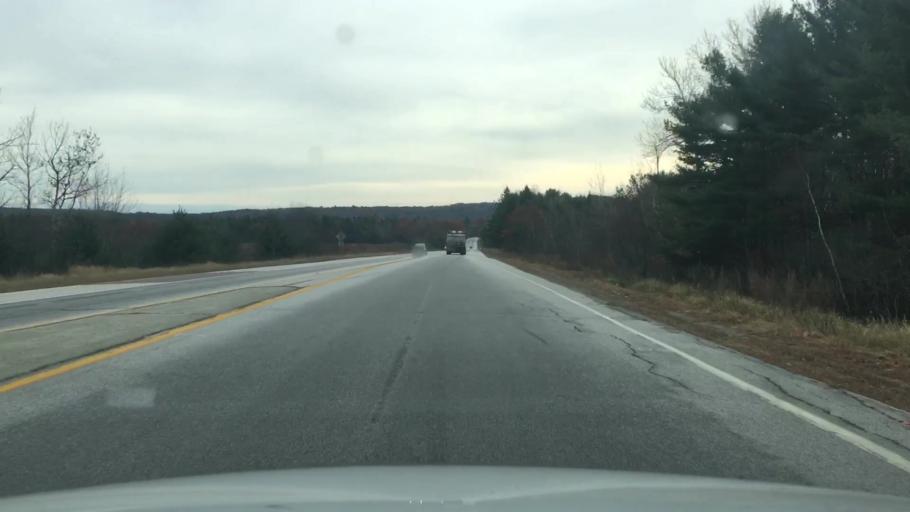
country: US
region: Maine
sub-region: Hancock County
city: Orland
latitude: 44.5724
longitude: -68.7289
